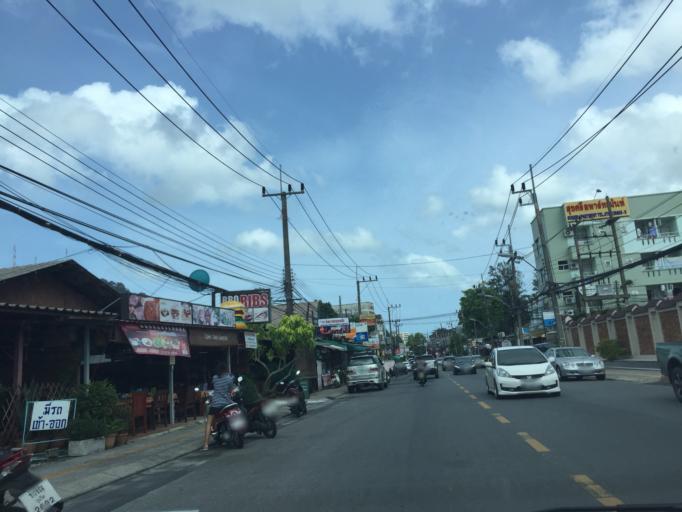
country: TH
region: Phuket
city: Wichit
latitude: 7.9014
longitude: 98.3810
